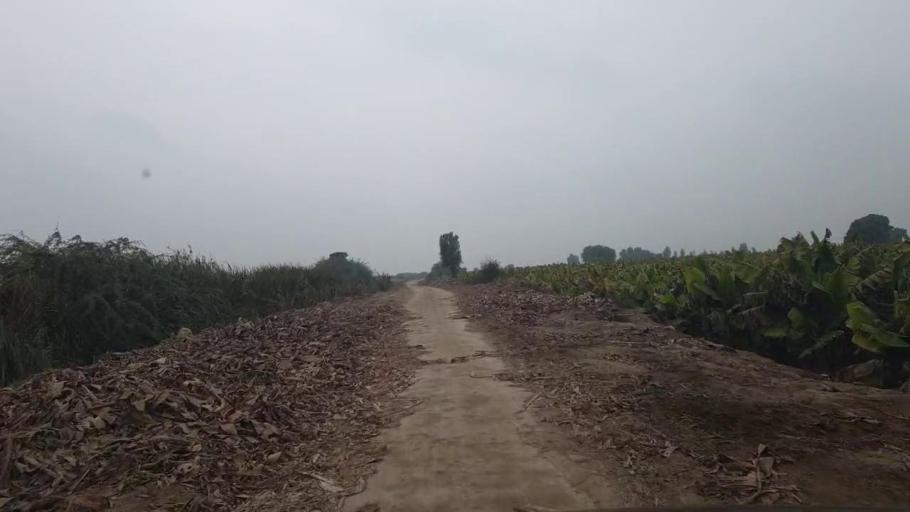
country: PK
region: Sindh
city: Tando Adam
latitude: 25.8465
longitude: 68.6786
